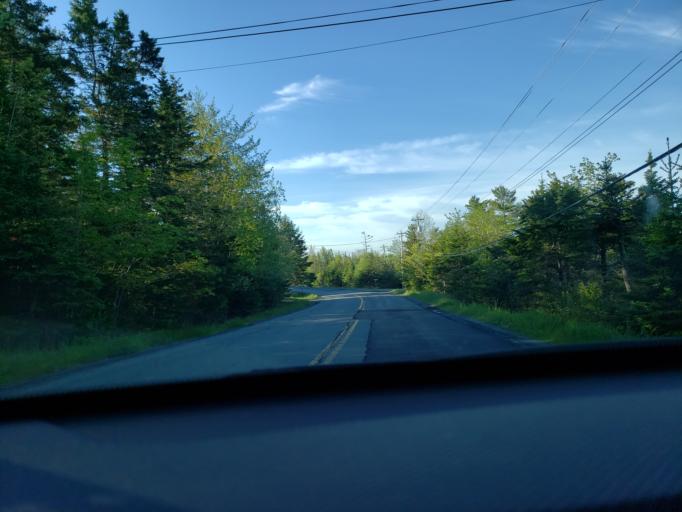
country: CA
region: Nova Scotia
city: Cole Harbour
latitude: 44.7159
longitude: -63.3974
